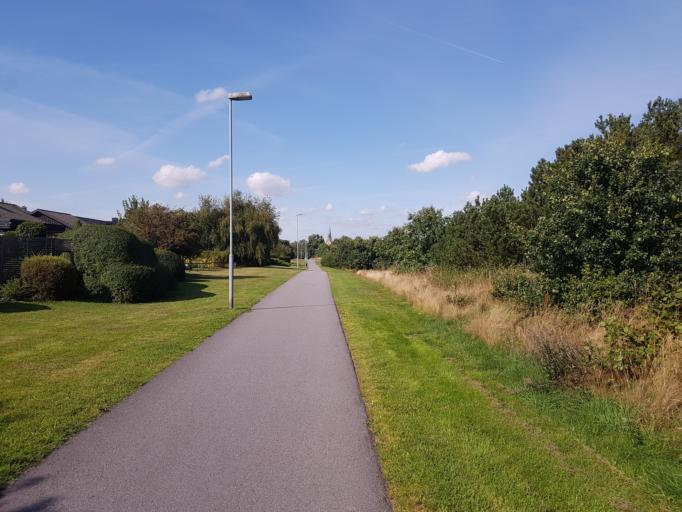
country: SE
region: Skane
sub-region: Sjobo Kommun
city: Sjoebo
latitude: 55.6391
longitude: 13.6997
